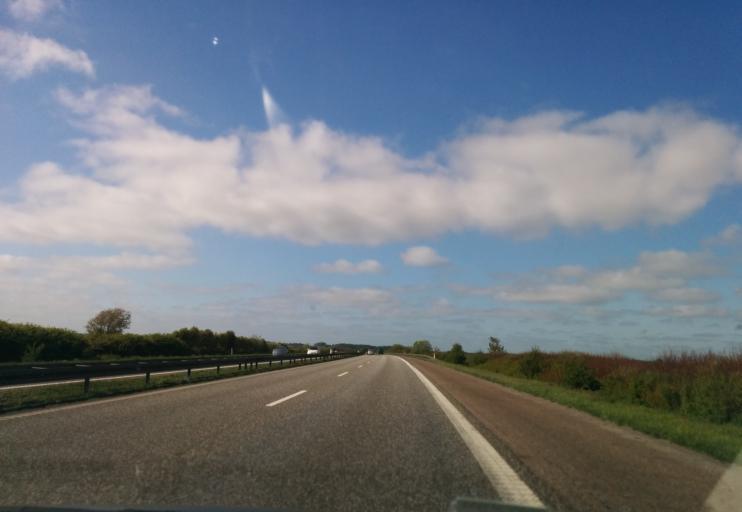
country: DK
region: South Denmark
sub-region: Fredericia Kommune
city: Taulov
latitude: 55.5754
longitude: 9.6149
